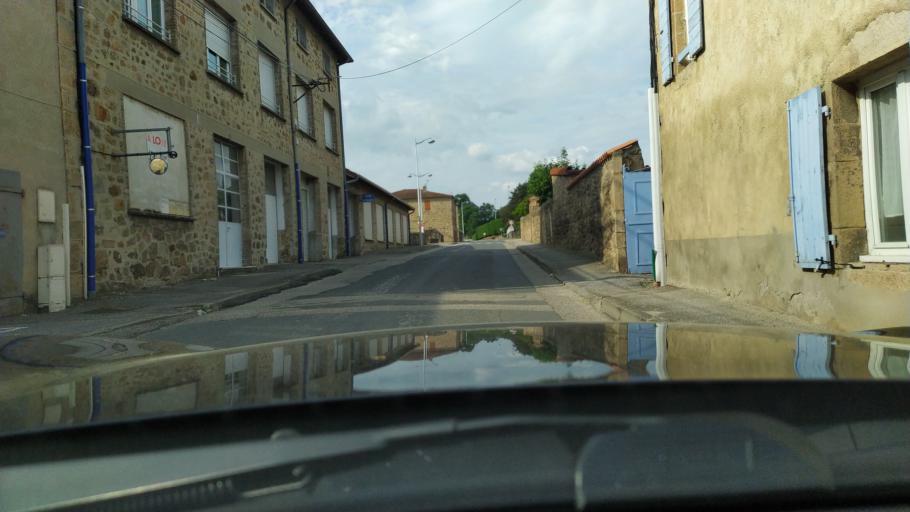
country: FR
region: Rhone-Alpes
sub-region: Departement de l'Ardeche
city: Peaugres
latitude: 45.2859
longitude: 4.7278
